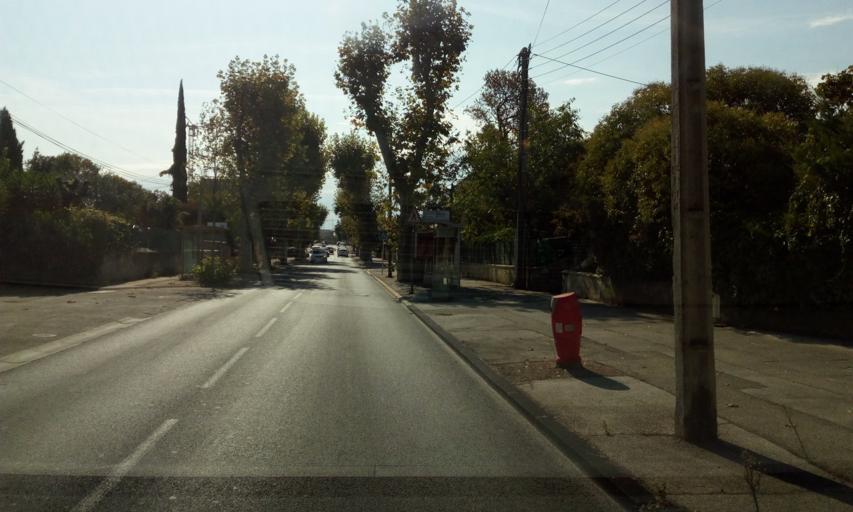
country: FR
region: Provence-Alpes-Cote d'Azur
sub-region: Departement du Var
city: La Valette-du-Var
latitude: 43.1211
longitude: 5.9753
